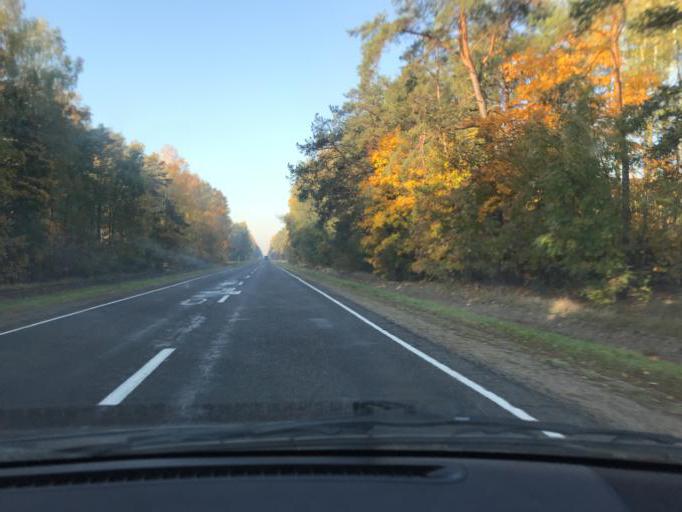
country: BY
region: Brest
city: Baranovichi
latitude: 52.9149
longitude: 25.9489
